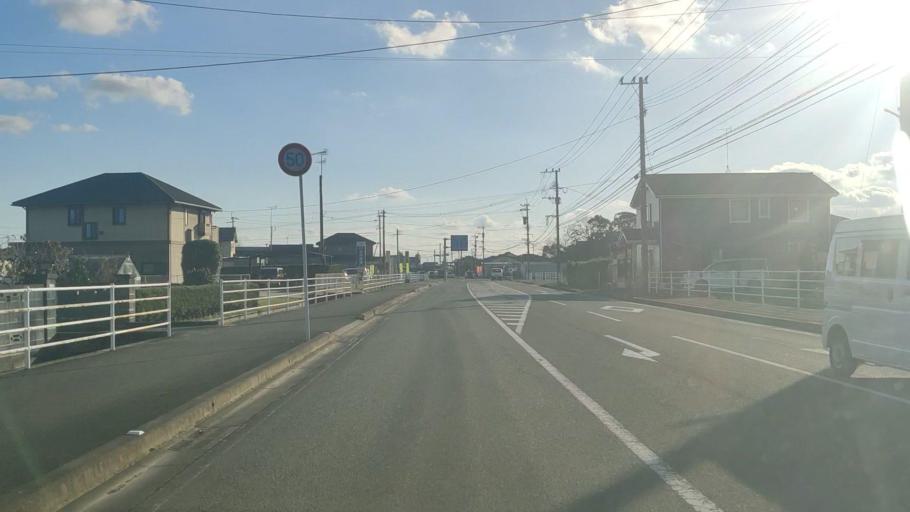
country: JP
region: Saga Prefecture
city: Saga-shi
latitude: 33.3112
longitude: 130.2649
